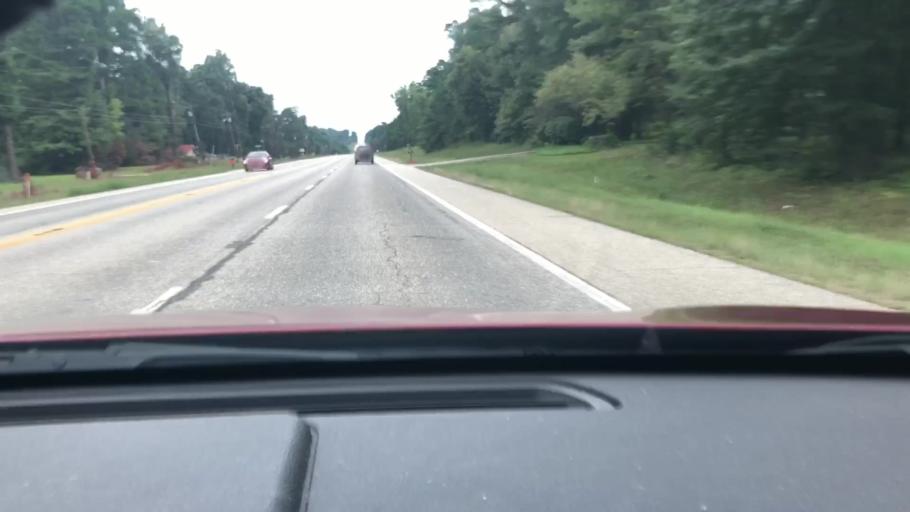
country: US
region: Arkansas
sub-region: Miller County
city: Texarkana
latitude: 33.4296
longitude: -93.9560
